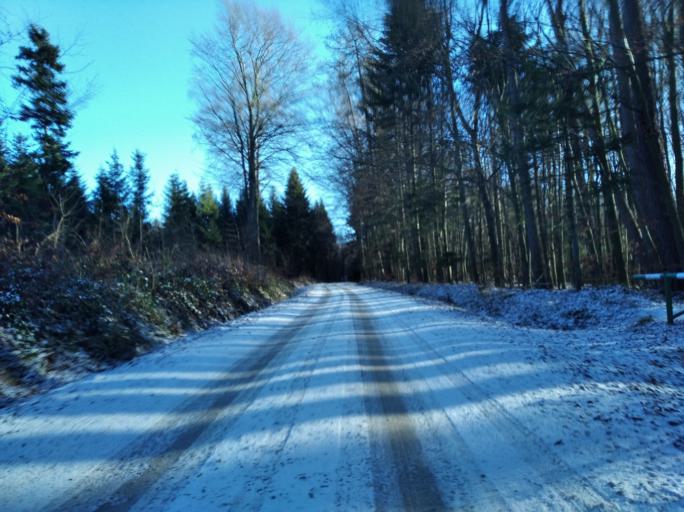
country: PL
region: Subcarpathian Voivodeship
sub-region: Powiat ropczycko-sedziszowski
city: Iwierzyce
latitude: 49.9722
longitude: 21.7695
